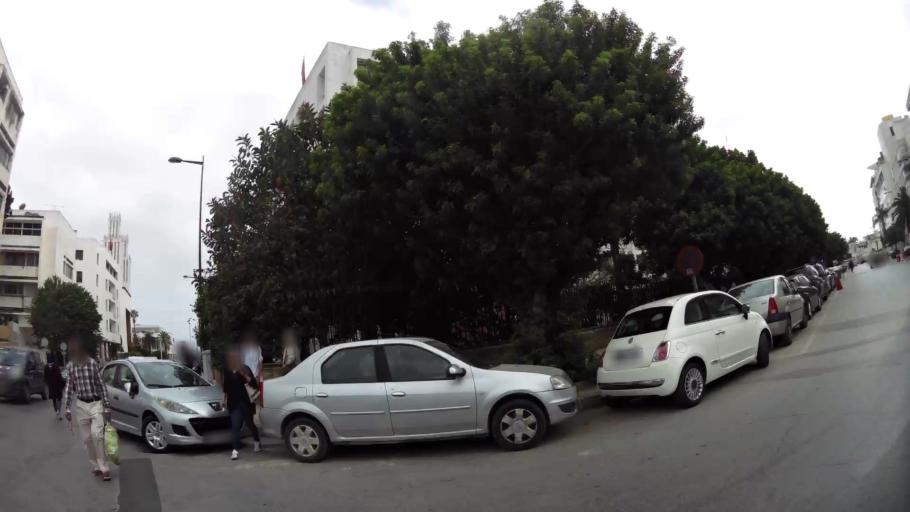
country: MA
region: Rabat-Sale-Zemmour-Zaer
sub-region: Rabat
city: Rabat
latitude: 34.0169
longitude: -6.8301
